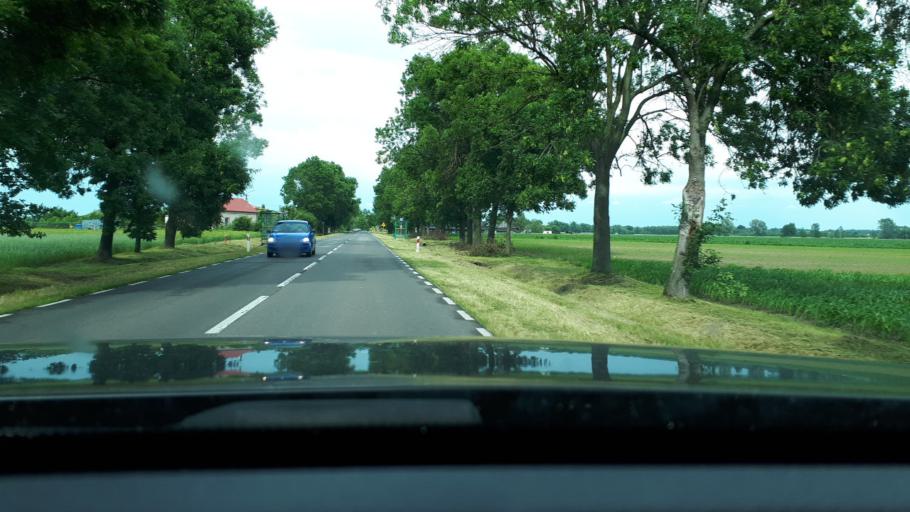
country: PL
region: Masovian Voivodeship
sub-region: Powiat sochaczewski
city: Paprotnia
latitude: 52.2625
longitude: 20.3627
